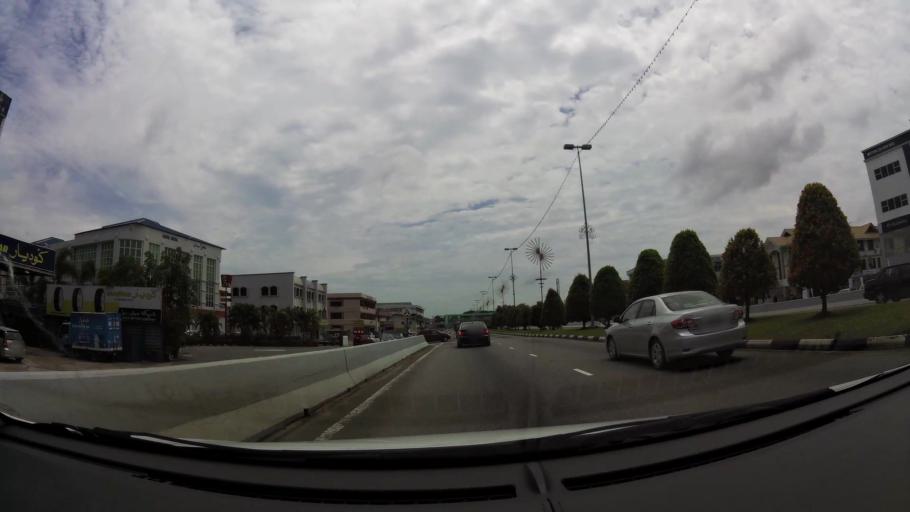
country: BN
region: Brunei and Muara
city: Bandar Seri Begawan
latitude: 4.9090
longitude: 114.9252
